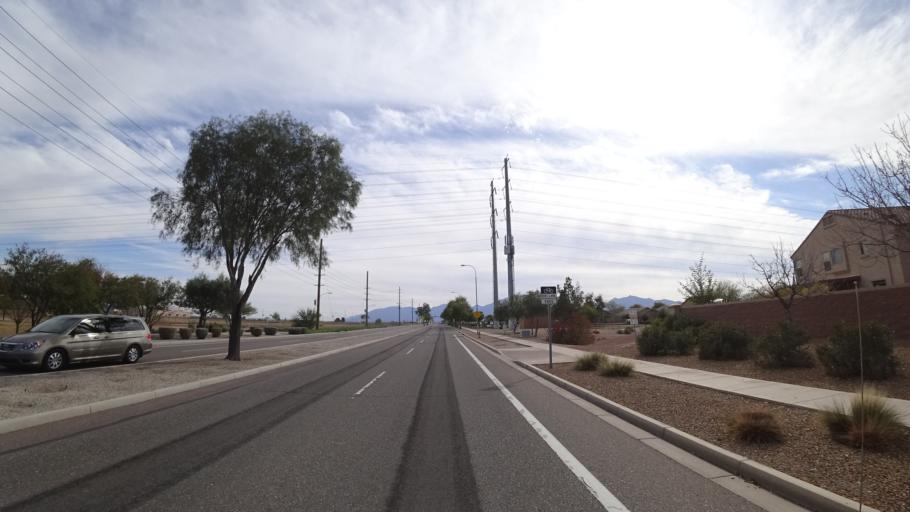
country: US
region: Arizona
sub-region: Maricopa County
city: Tolleson
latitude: 33.4146
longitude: -112.2555
